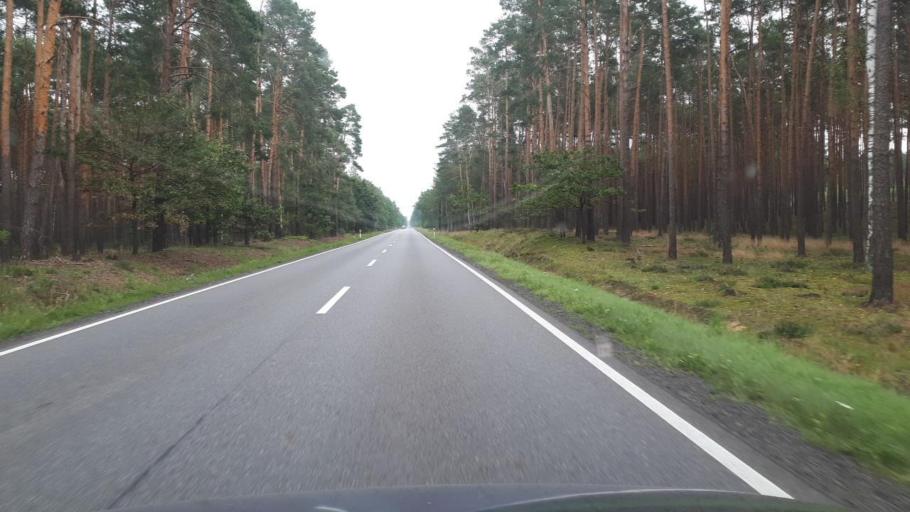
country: PL
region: Greater Poland Voivodeship
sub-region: Powiat ostrowski
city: Przygodzice
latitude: 51.5015
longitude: 17.7994
